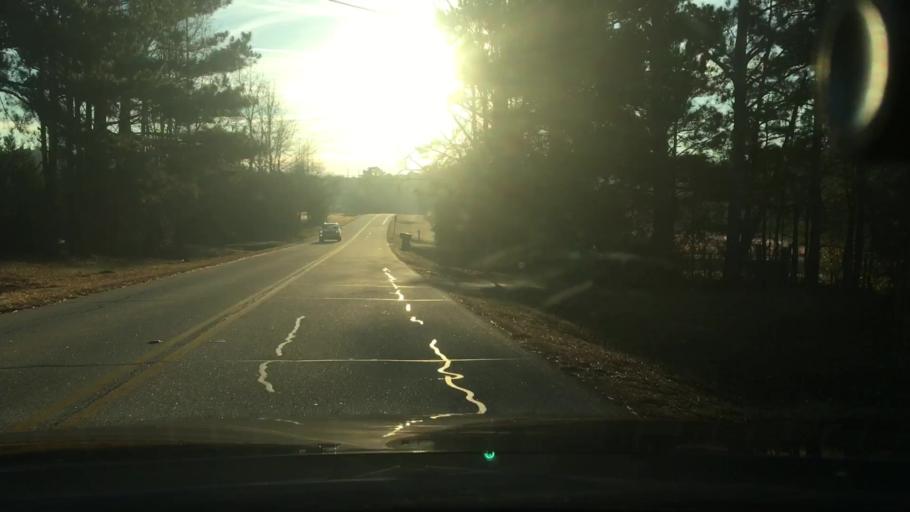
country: US
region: Georgia
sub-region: Coweta County
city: Senoia
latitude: 33.3219
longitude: -84.4879
